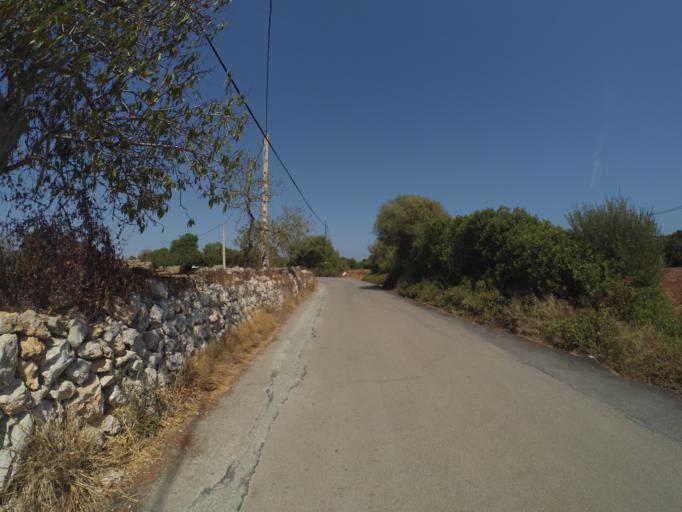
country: ES
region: Balearic Islands
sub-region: Illes Balears
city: Santanyi
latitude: 39.3934
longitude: 3.2372
